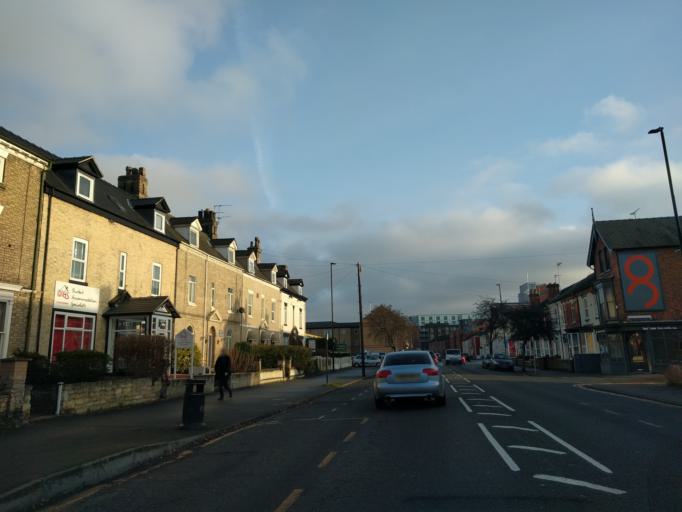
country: GB
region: England
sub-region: Lincolnshire
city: Lincoln
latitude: 53.2317
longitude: -0.5520
